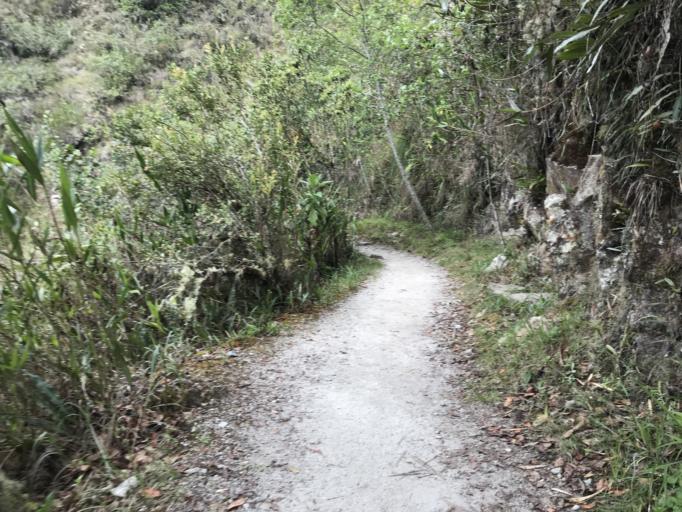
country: PE
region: Cusco
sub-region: Provincia de La Convencion
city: Santa Teresa
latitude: -13.1822
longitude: -72.5405
